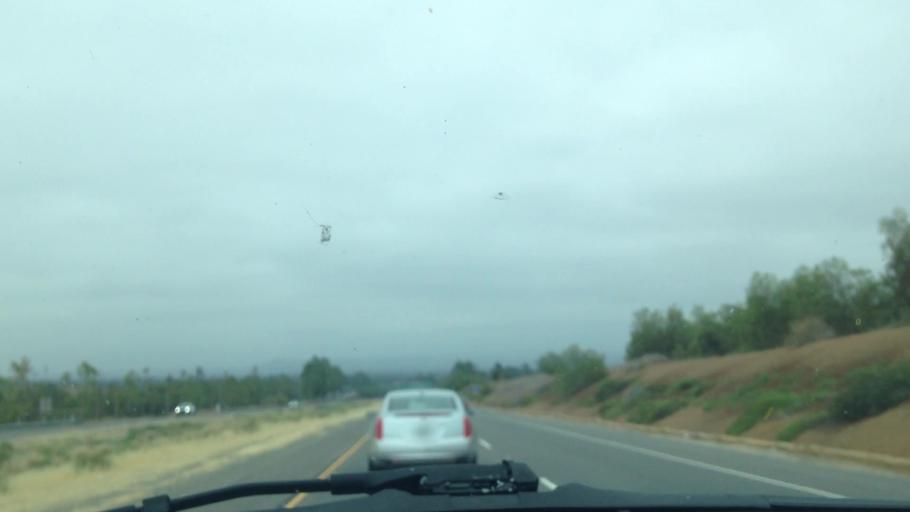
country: US
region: California
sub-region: Orange County
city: North Tustin
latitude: 33.7510
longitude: -117.7646
